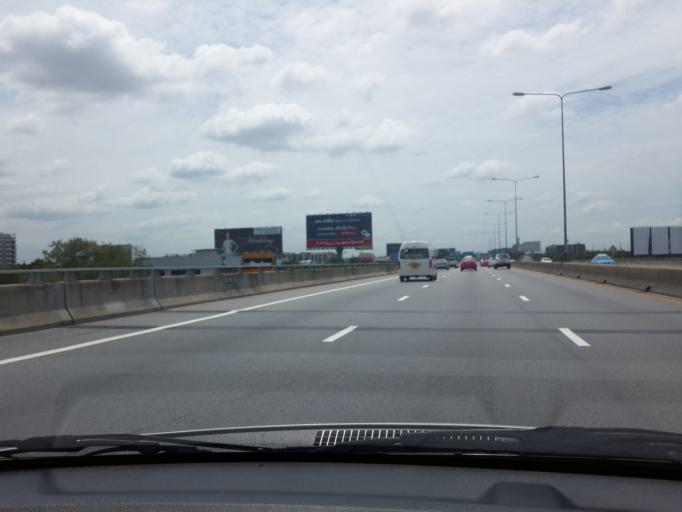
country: TH
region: Bangkok
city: Suan Luang
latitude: 13.7426
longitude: 100.6368
